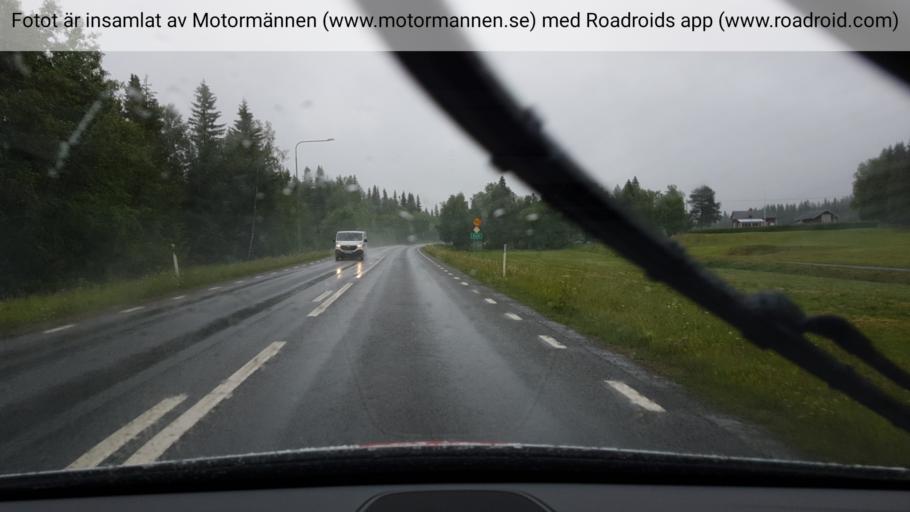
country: SE
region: Jaemtland
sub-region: OEstersunds Kommun
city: Lit
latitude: 63.4349
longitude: 15.1233
